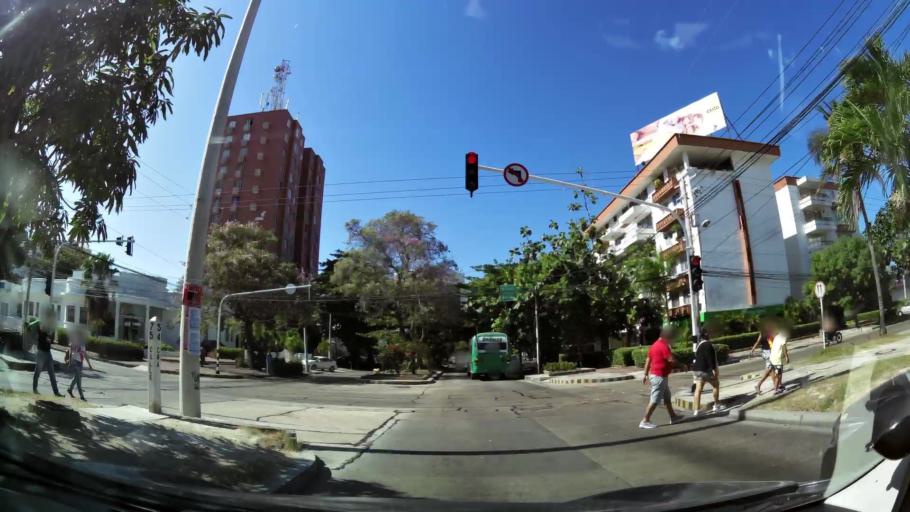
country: CO
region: Atlantico
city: Barranquilla
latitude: 11.0018
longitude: -74.8038
